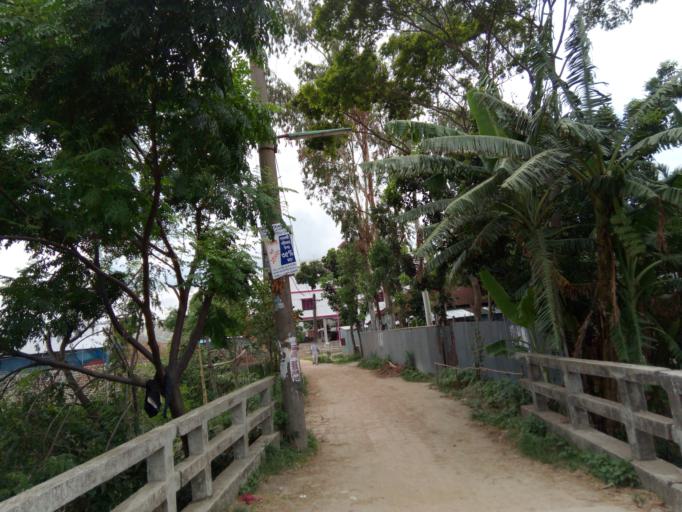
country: BD
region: Dhaka
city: Paltan
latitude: 23.7602
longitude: 90.4742
